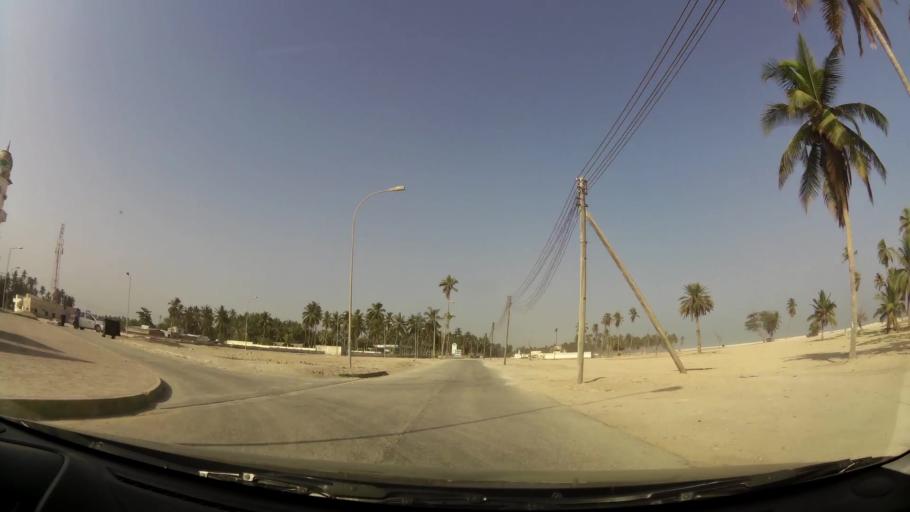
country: OM
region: Zufar
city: Salalah
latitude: 17.0024
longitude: 54.1114
